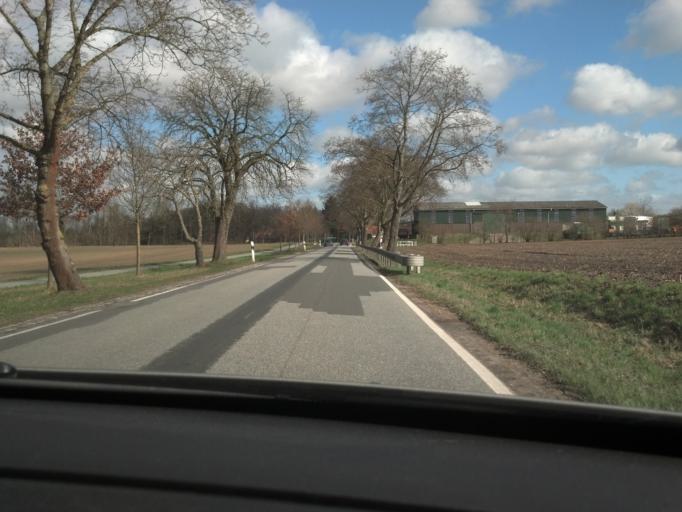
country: DE
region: Mecklenburg-Vorpommern
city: Boizenburg
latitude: 53.4216
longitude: 10.7460
